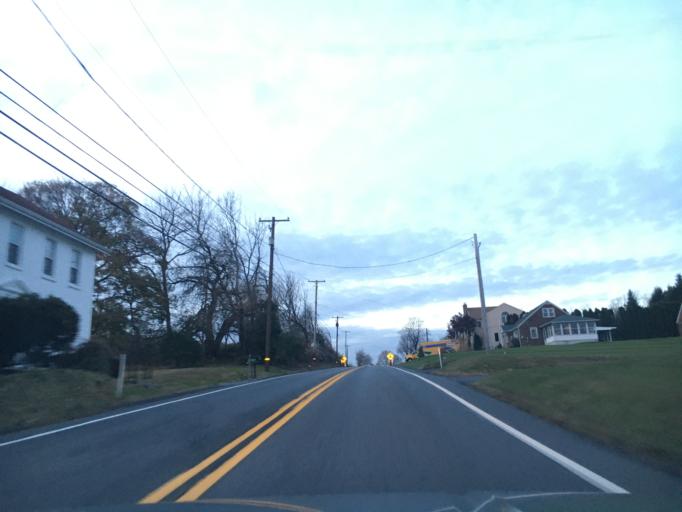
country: US
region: Pennsylvania
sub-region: Lehigh County
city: Schnecksville
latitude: 40.6763
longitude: -75.5695
